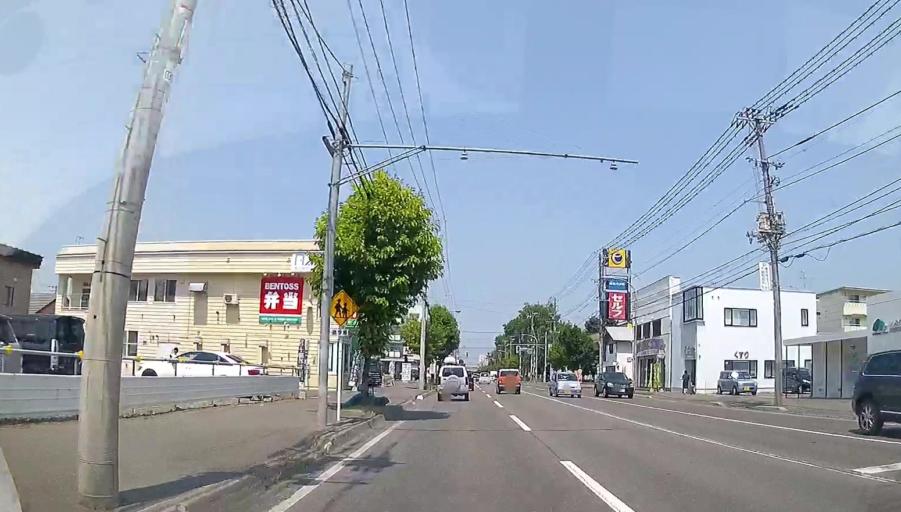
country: JP
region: Hokkaido
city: Obihiro
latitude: 42.9036
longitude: 143.1998
